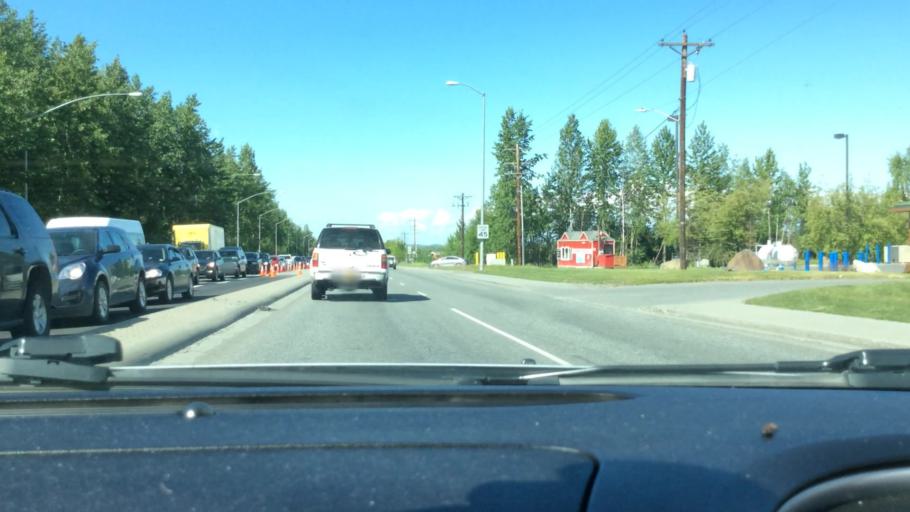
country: US
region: Alaska
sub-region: Anchorage Municipality
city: Anchorage
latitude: 61.2099
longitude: -149.7784
